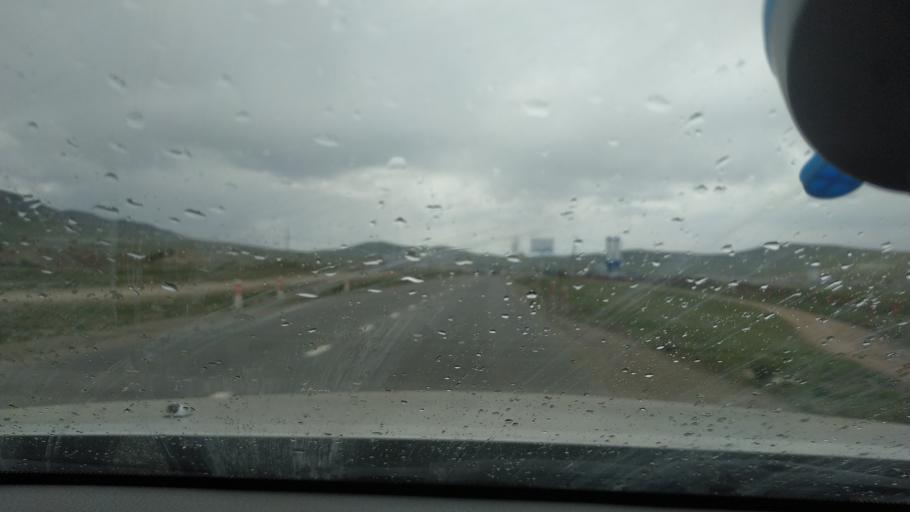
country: MN
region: Ulaanbaatar
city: Ulaanbaatar
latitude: 47.8230
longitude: 106.7638
